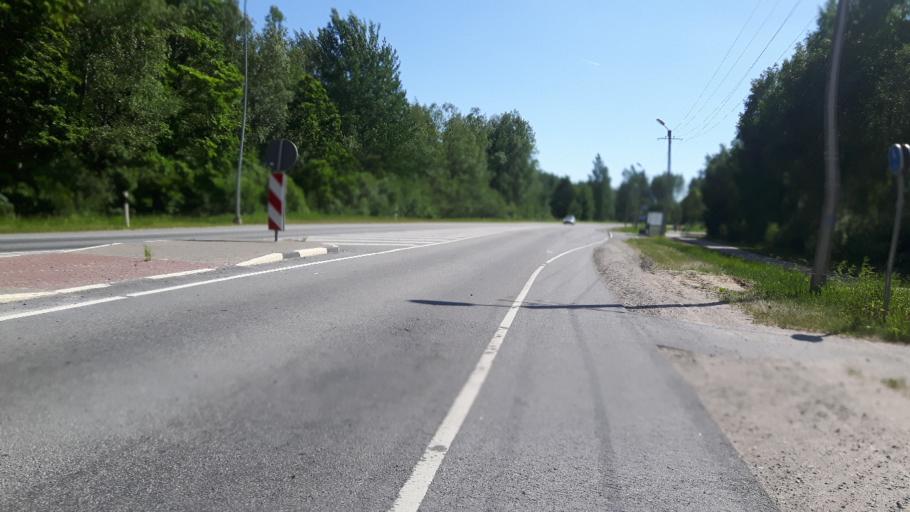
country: EE
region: Paernumaa
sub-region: Paikuse vald
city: Paikuse
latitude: 58.3872
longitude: 24.6400
